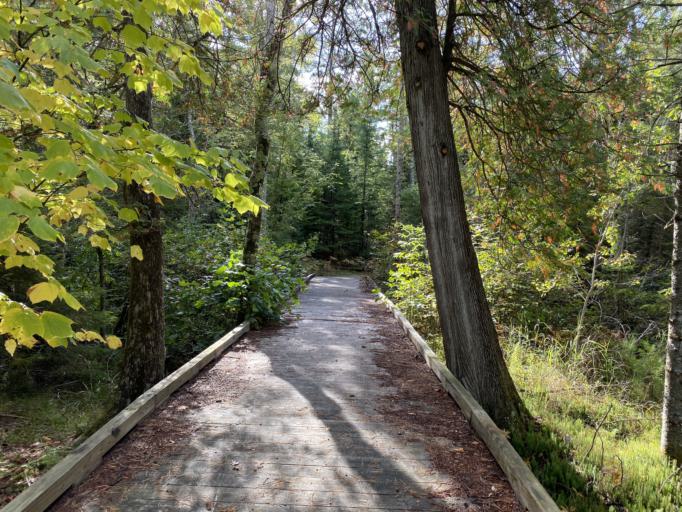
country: US
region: Michigan
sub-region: Mackinac County
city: Saint Ignace
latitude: 45.7452
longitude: -84.8930
